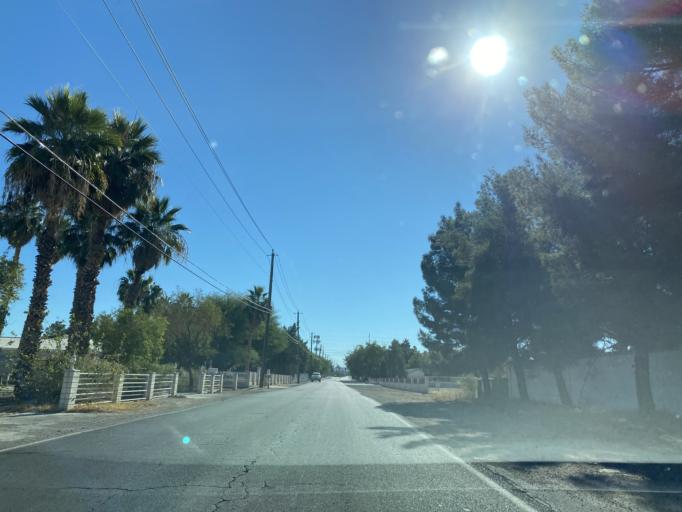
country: US
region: Nevada
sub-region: Clark County
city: Whitney
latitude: 36.0884
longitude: -115.0868
